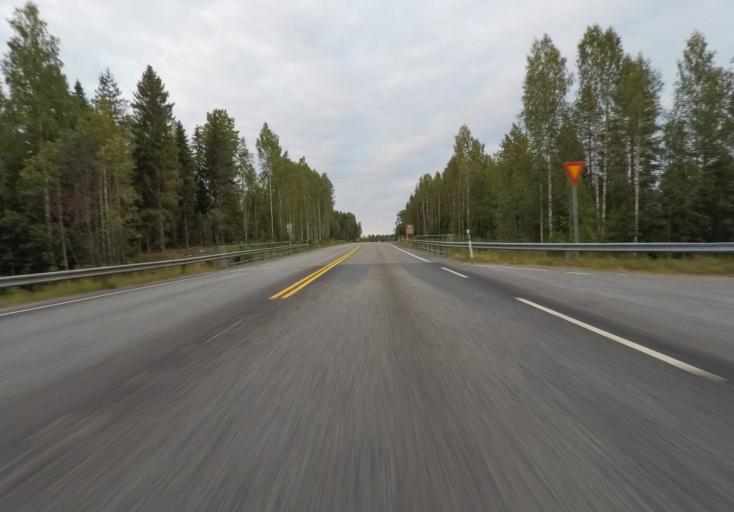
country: FI
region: Central Finland
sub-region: Jyvaeskylae
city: Hankasalmi
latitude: 62.2809
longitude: 26.3395
